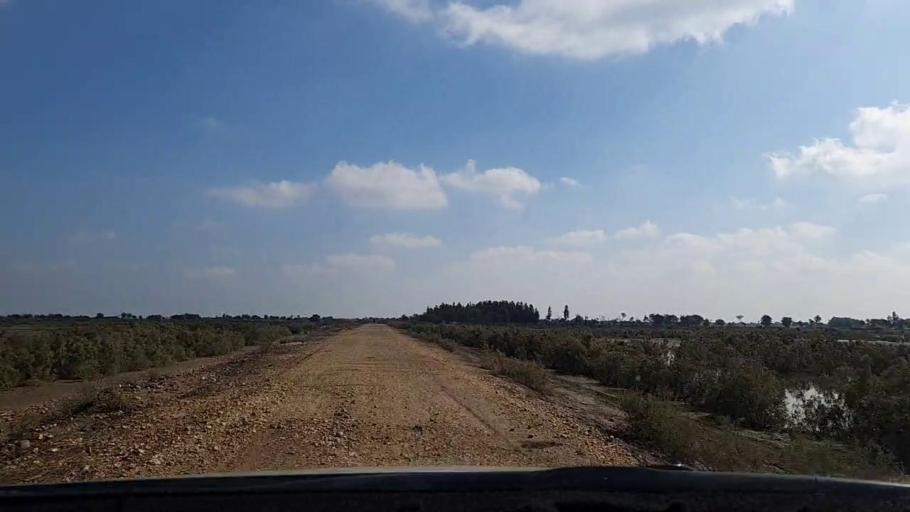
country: PK
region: Sindh
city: Pithoro
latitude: 25.7320
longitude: 69.2839
